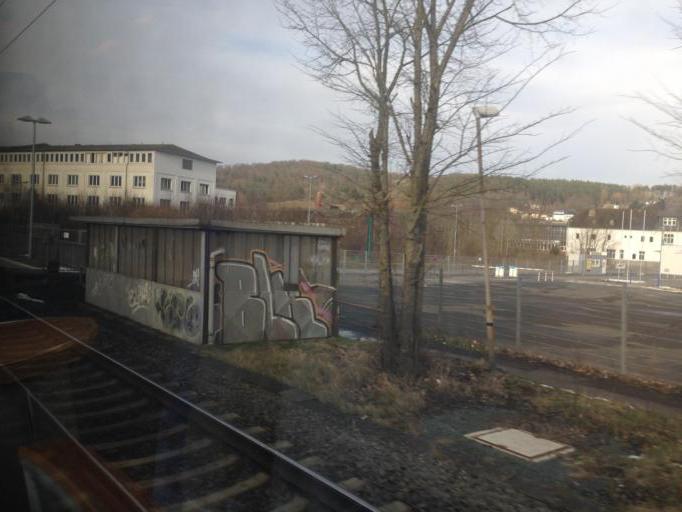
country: DE
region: Hesse
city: Herborn
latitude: 50.6996
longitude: 8.3079
